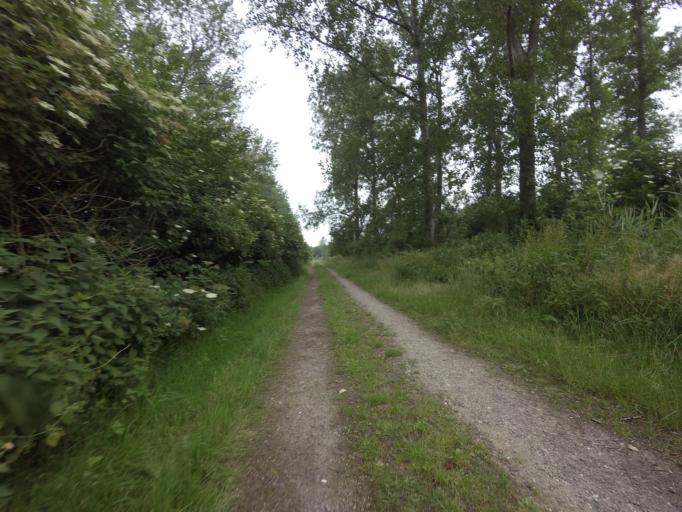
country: NL
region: Flevoland
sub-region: Gemeente Almere
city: Almere Stad
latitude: 52.4079
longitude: 5.3309
